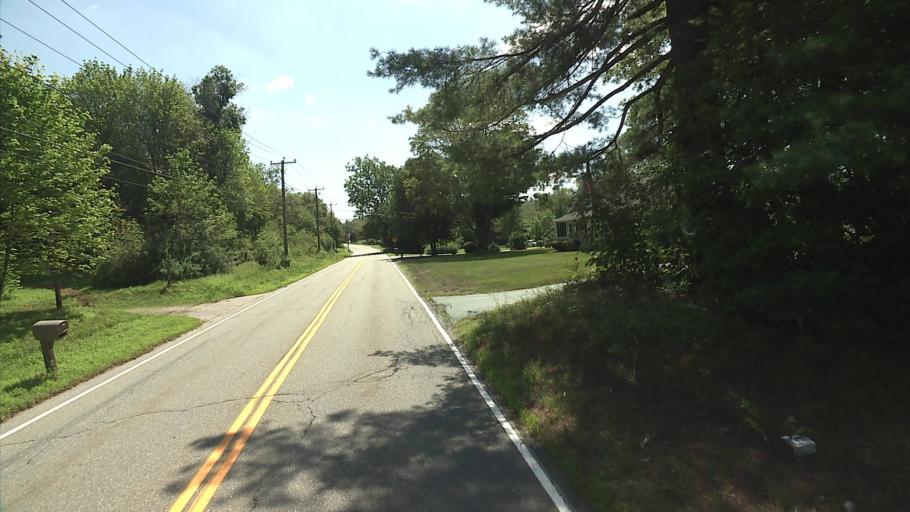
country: US
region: Connecticut
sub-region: Windham County
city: Plainfield Village
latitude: 41.6870
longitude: -71.9435
